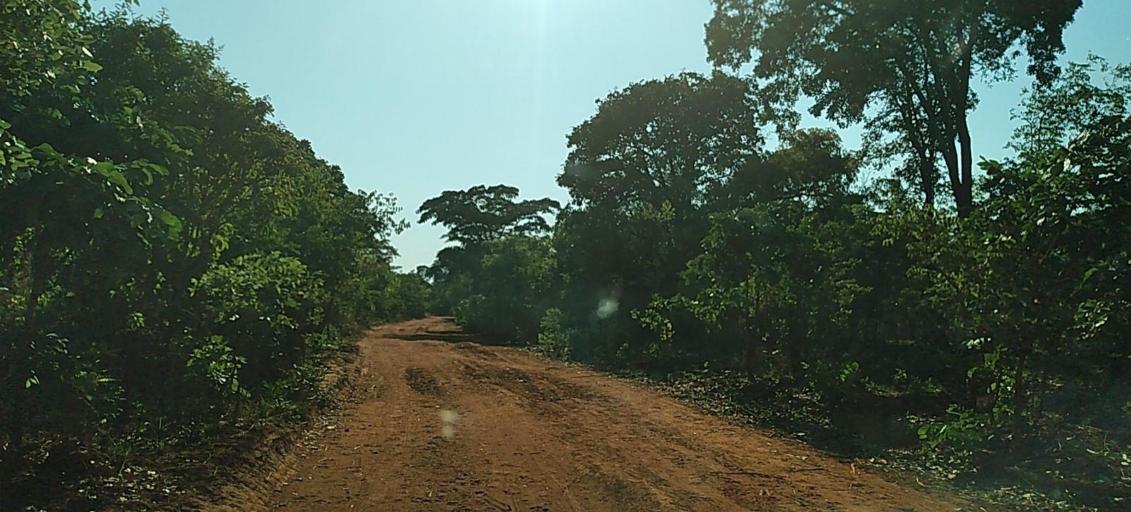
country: ZM
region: Copperbelt
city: Luanshya
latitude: -13.4591
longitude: 28.8182
